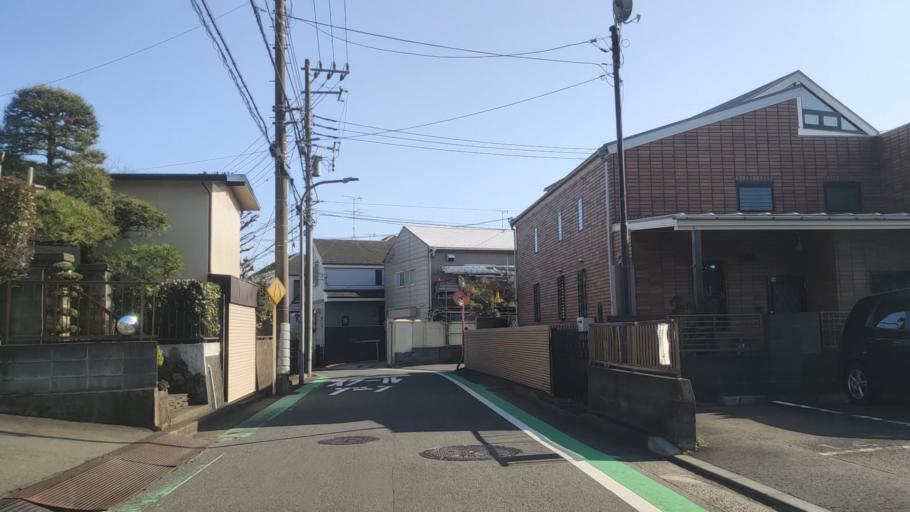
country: JP
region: Kanagawa
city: Yokohama
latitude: 35.4662
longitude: 139.5970
